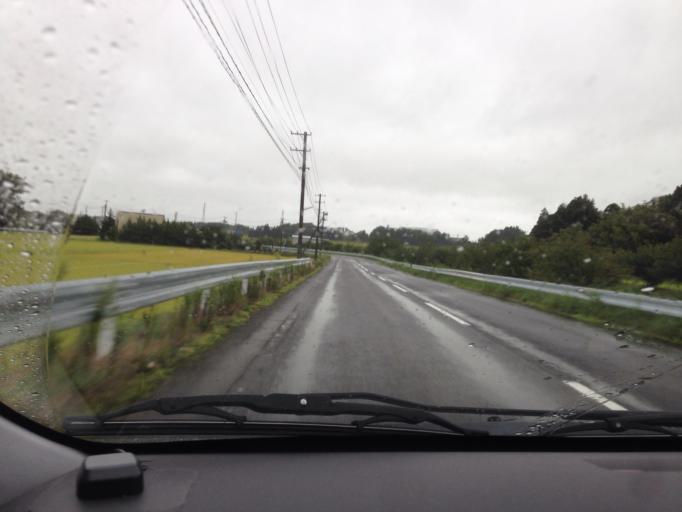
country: JP
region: Fukushima
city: Koriyama
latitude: 37.4536
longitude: 140.2855
